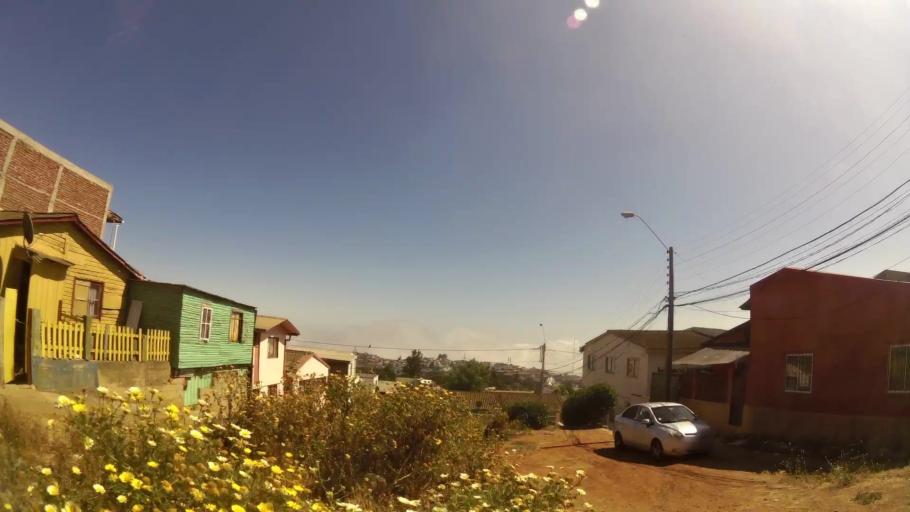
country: CL
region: Valparaiso
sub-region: Provincia de Valparaiso
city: Valparaiso
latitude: -33.0465
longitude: -71.6480
